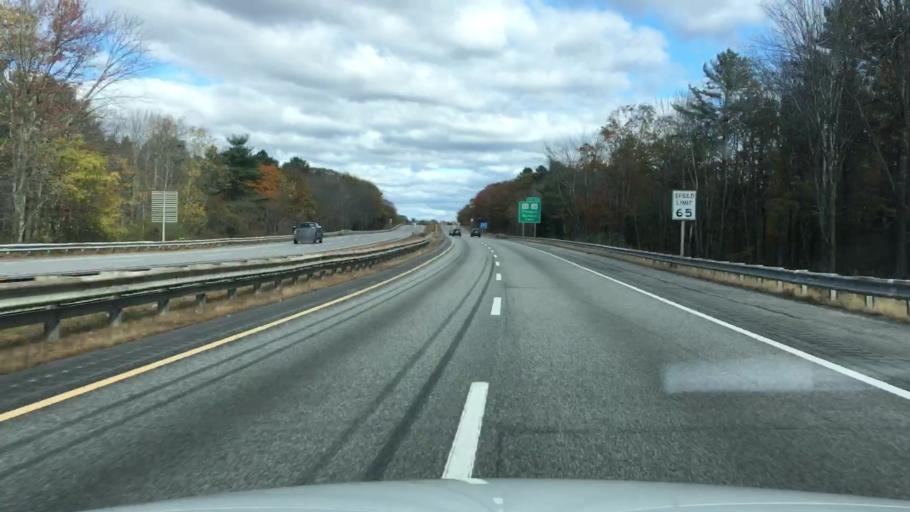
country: US
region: Maine
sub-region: Cumberland County
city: Freeport
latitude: 43.8506
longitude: -70.1154
